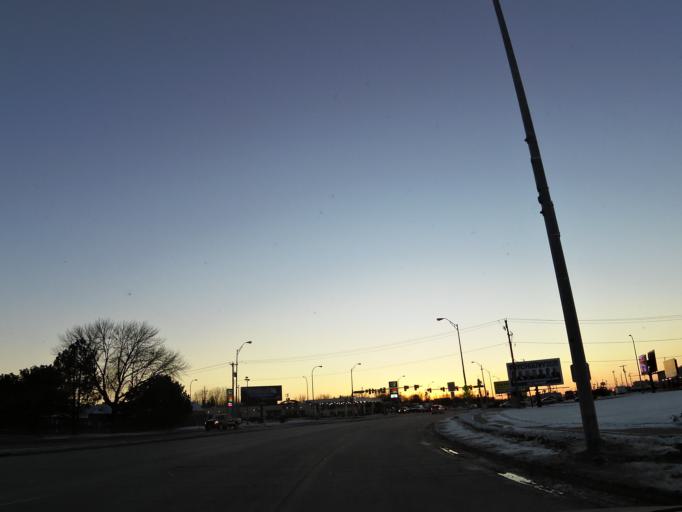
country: US
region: North Dakota
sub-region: Grand Forks County
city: Grand Forks
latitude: 47.9167
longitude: -97.0433
